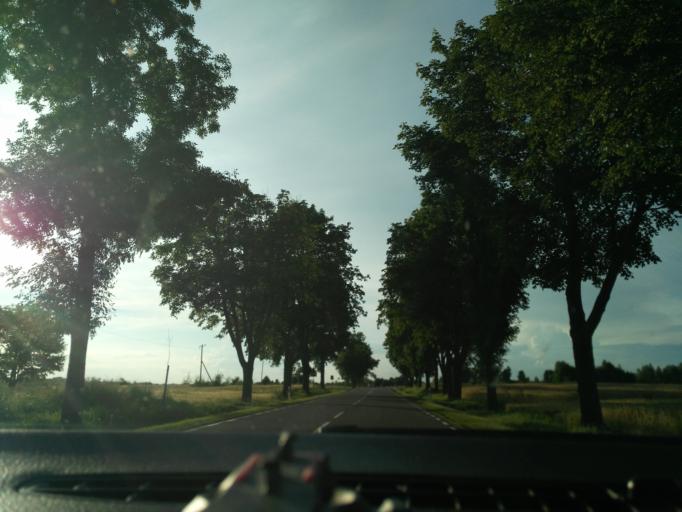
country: PL
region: Lublin Voivodeship
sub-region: Powiat krasnicki
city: Krasnik
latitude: 50.8797
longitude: 22.2631
